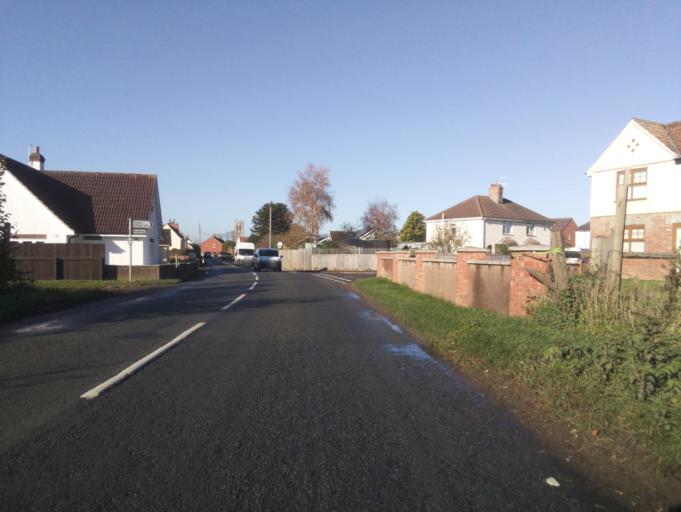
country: GB
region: England
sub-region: Somerset
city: Westonzoyland
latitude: 51.1076
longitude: -2.9207
